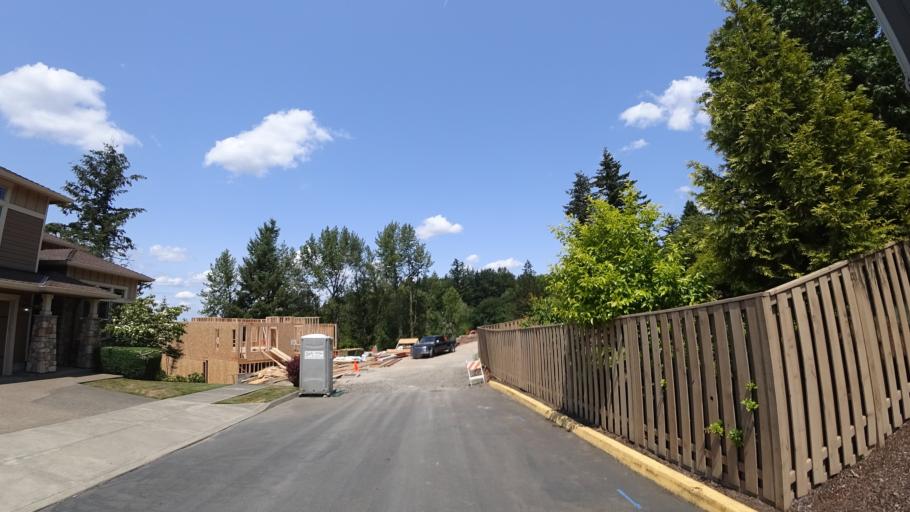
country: US
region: Oregon
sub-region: Clackamas County
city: Happy Valley
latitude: 45.4467
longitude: -122.5527
